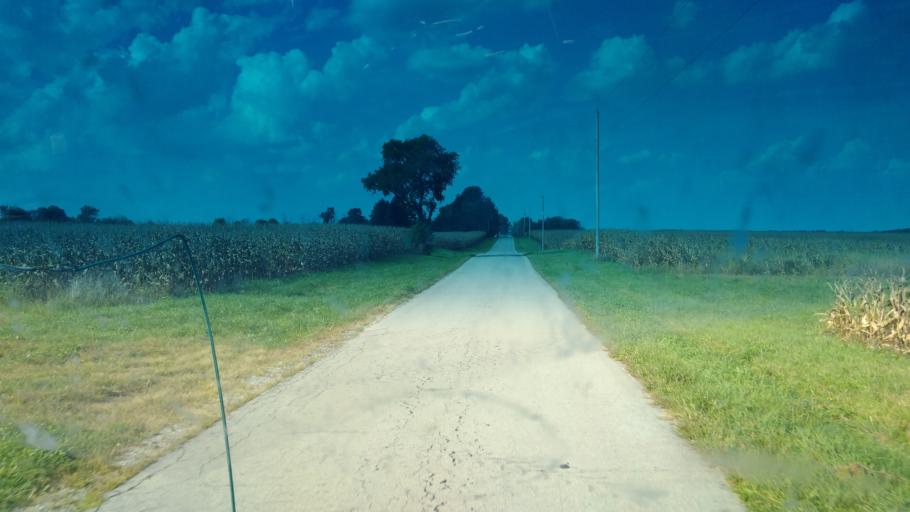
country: US
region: Ohio
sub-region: Hardin County
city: Forest
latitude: 40.8369
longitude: -83.5762
